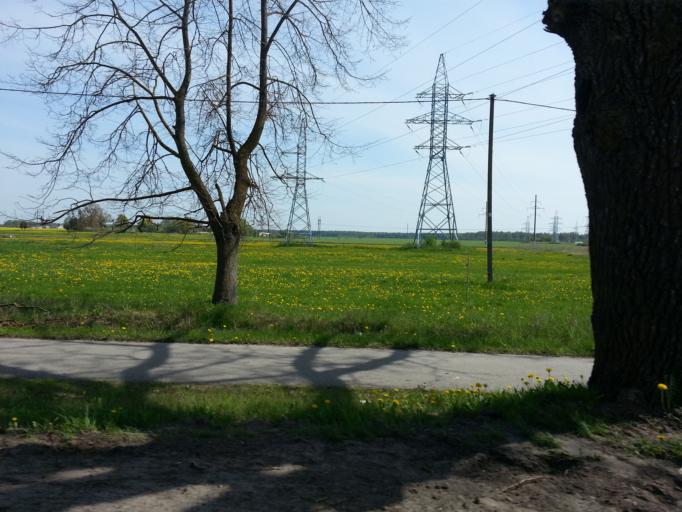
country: LT
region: Panevezys
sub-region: Panevezys City
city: Panevezys
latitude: 55.7650
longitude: 24.3000
